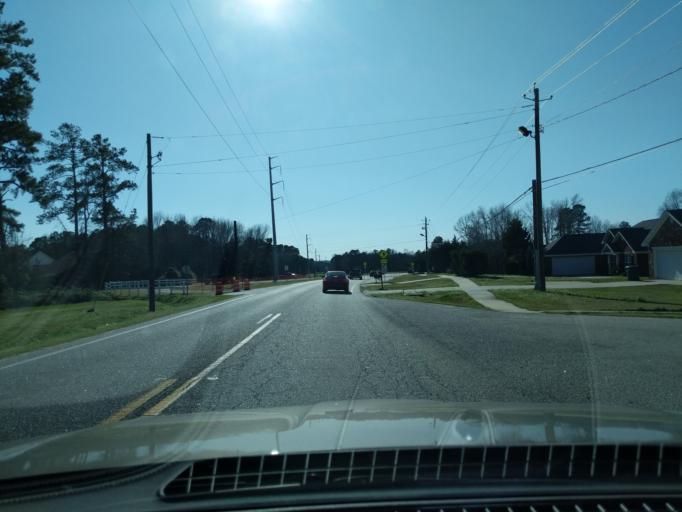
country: US
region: Georgia
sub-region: Columbia County
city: Grovetown
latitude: 33.4523
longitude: -82.2120
